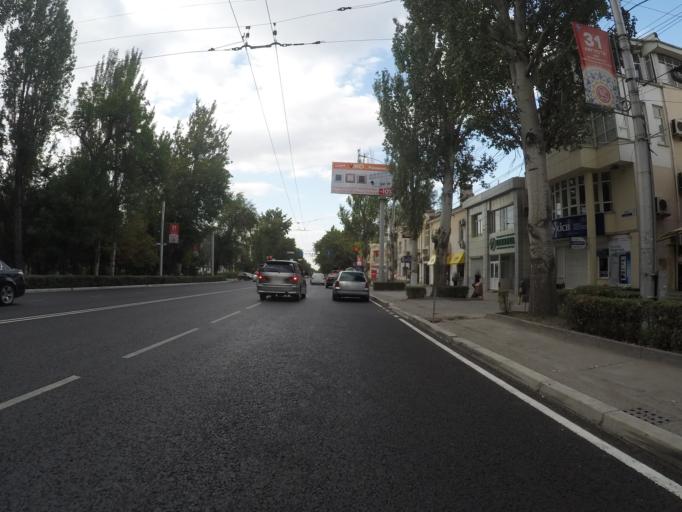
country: KG
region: Chuy
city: Bishkek
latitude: 42.8695
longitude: 74.5877
